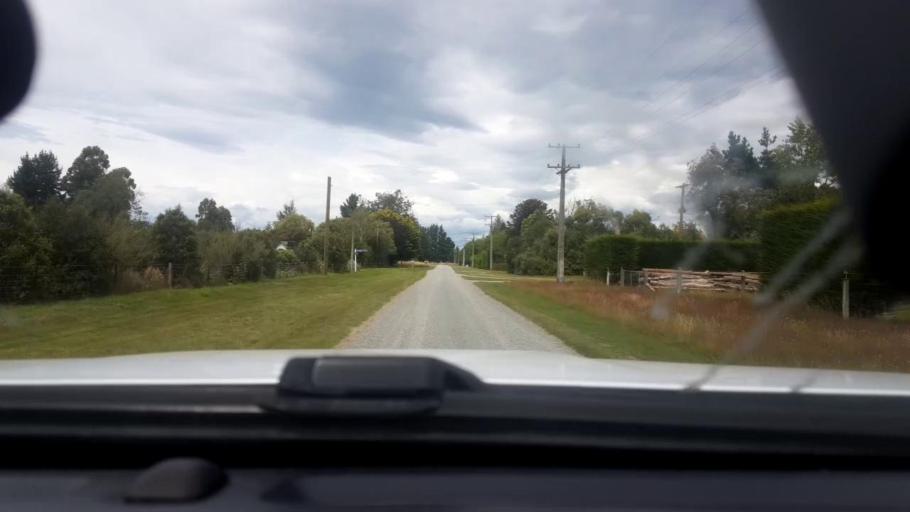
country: NZ
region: Canterbury
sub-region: Timaru District
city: Pleasant Point
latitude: -44.1416
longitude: 171.2899
